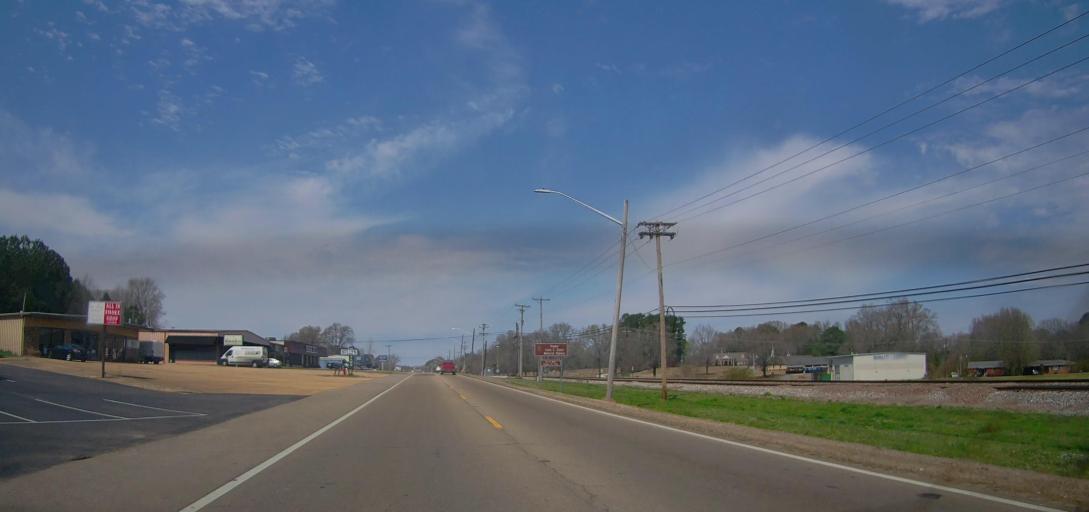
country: US
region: Mississippi
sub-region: Union County
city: New Albany
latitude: 34.5024
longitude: -89.0270
